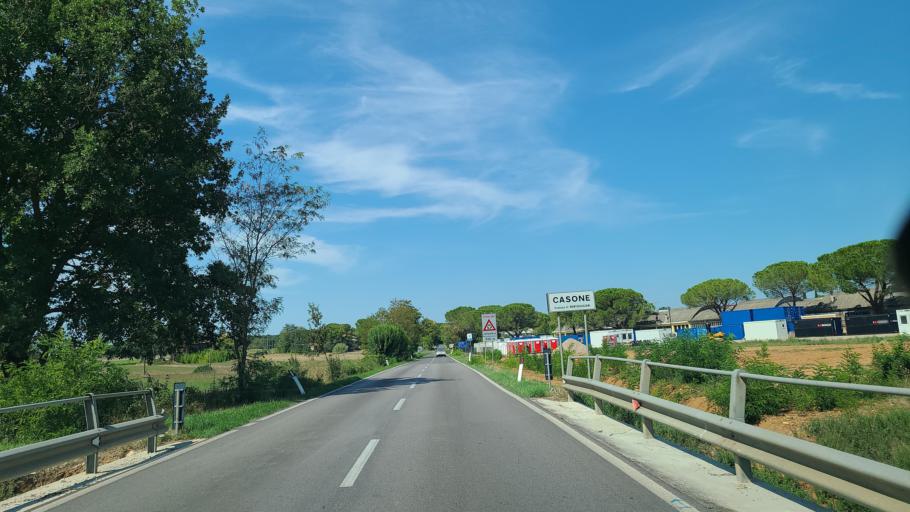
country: IT
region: Tuscany
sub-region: Provincia di Siena
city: Castellina Scalo
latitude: 43.3932
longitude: 11.1950
